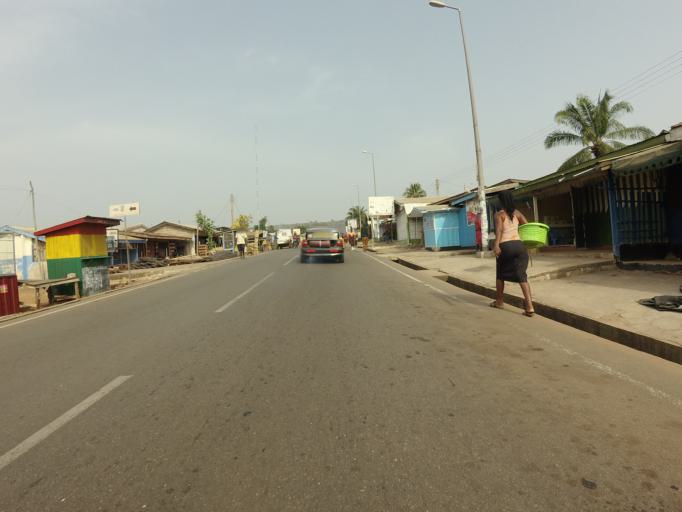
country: GH
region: Volta
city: Ho
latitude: 6.6151
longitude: 0.4741
